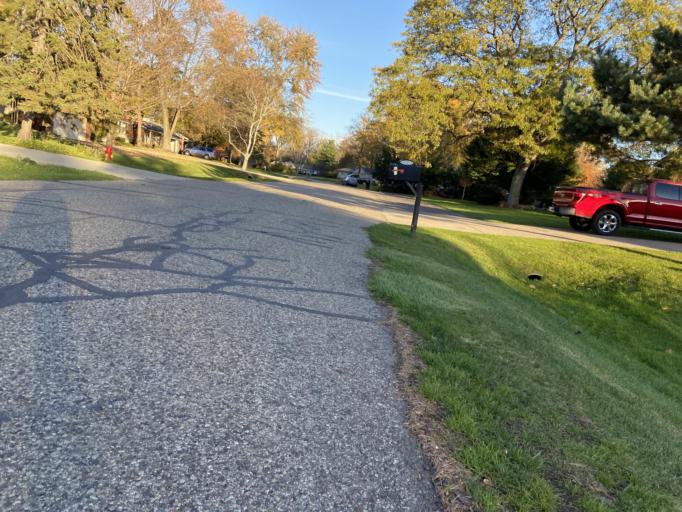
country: US
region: Michigan
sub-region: Oakland County
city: Farmington Hills
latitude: 42.5012
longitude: -83.3665
